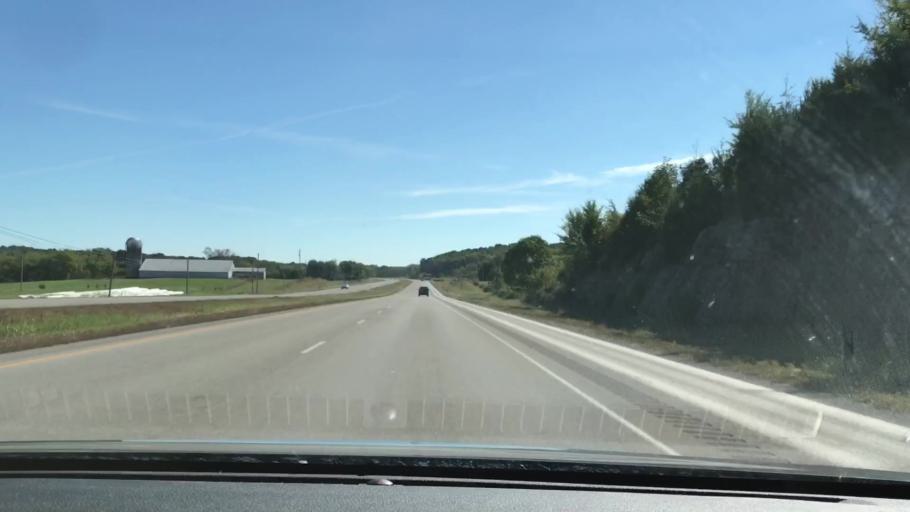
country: US
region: Kentucky
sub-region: Christian County
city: Hopkinsville
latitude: 36.8488
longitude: -87.3397
